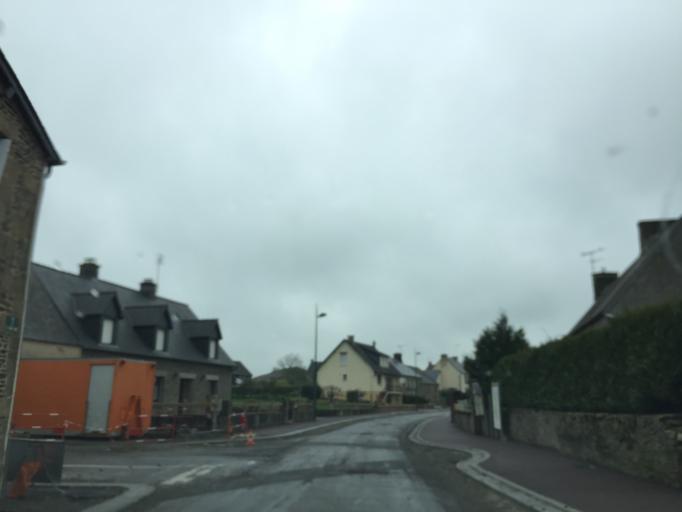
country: FR
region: Lower Normandy
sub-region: Departement de la Manche
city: Pontorson
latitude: 48.5778
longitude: -1.4512
